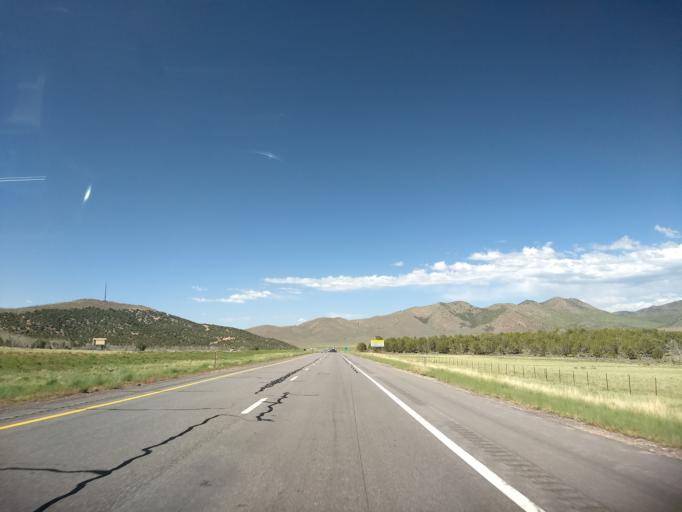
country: US
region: Utah
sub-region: Beaver County
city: Beaver
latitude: 38.6506
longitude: -112.5998
